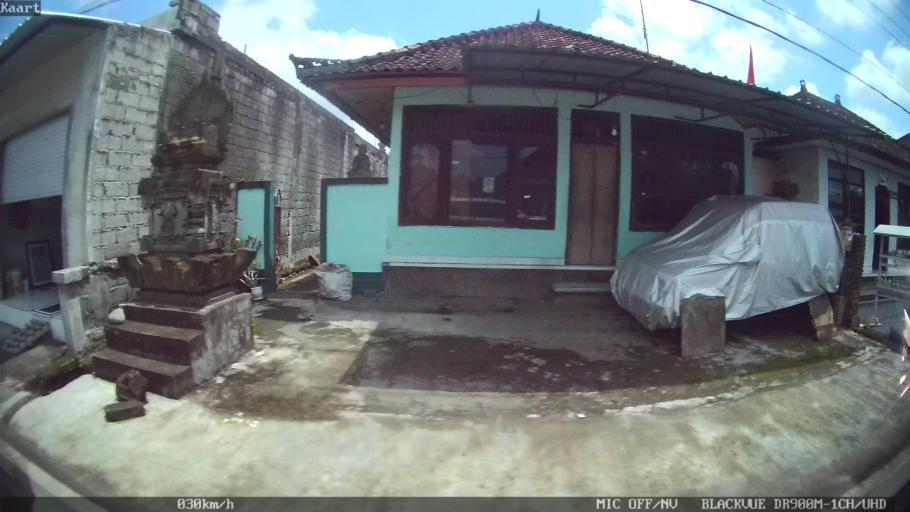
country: ID
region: Bali
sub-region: Kabupaten Gianyar
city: Ubud
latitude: -8.5312
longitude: 115.2823
